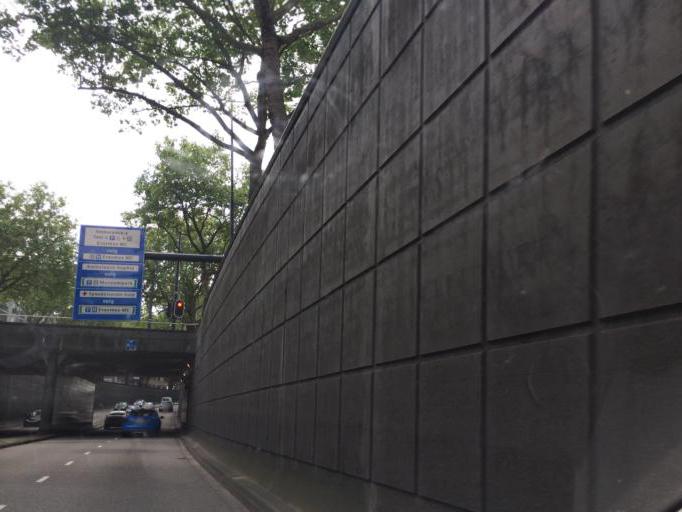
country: NL
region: South Holland
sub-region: Gemeente Rotterdam
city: Delfshaven
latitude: 51.9143
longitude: 4.4636
